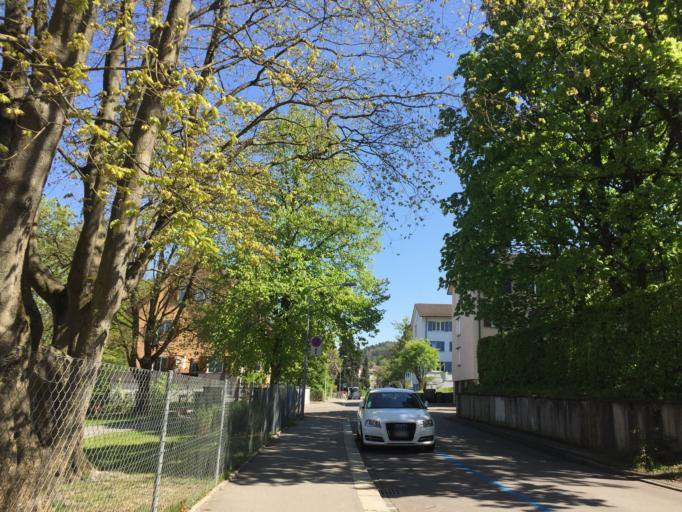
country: CH
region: Zurich
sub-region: Bezirk Zuerich
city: Zuerich (Kreis 11) / Oerlikon
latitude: 47.4067
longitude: 8.5536
